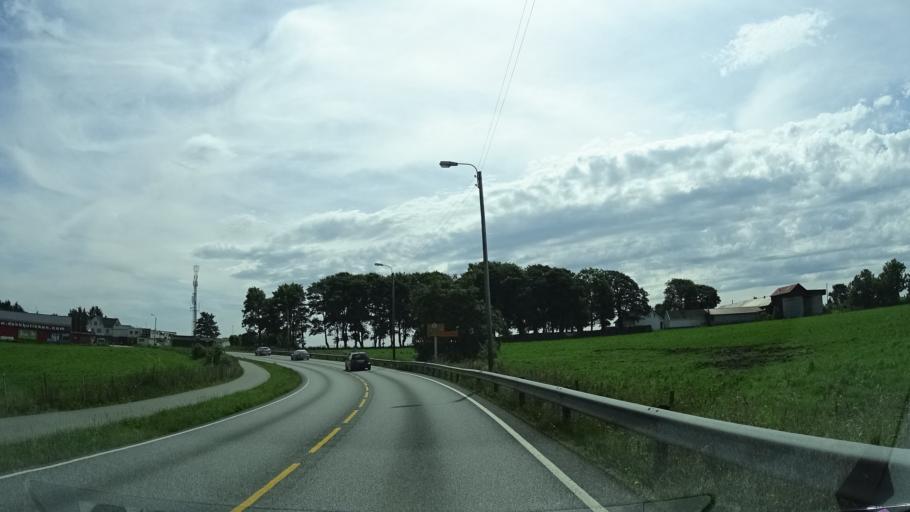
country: NO
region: Rogaland
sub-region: Randaberg
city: Randaberg
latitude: 58.9843
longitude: 5.6662
